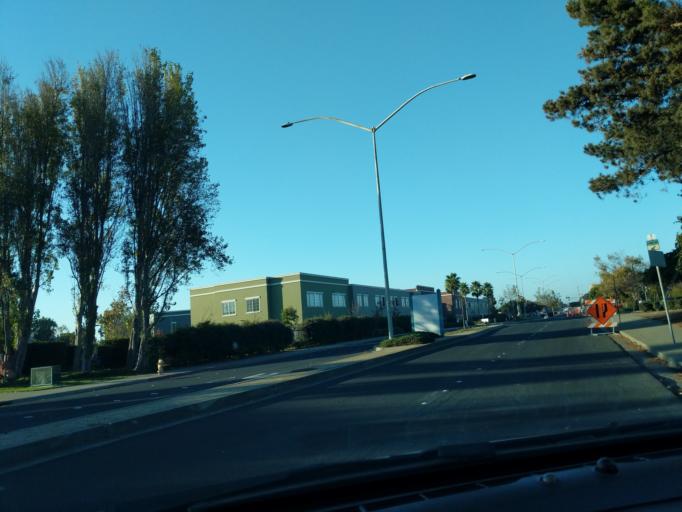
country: US
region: California
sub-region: Contra Costa County
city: Richmond
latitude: 37.9176
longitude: -122.3558
